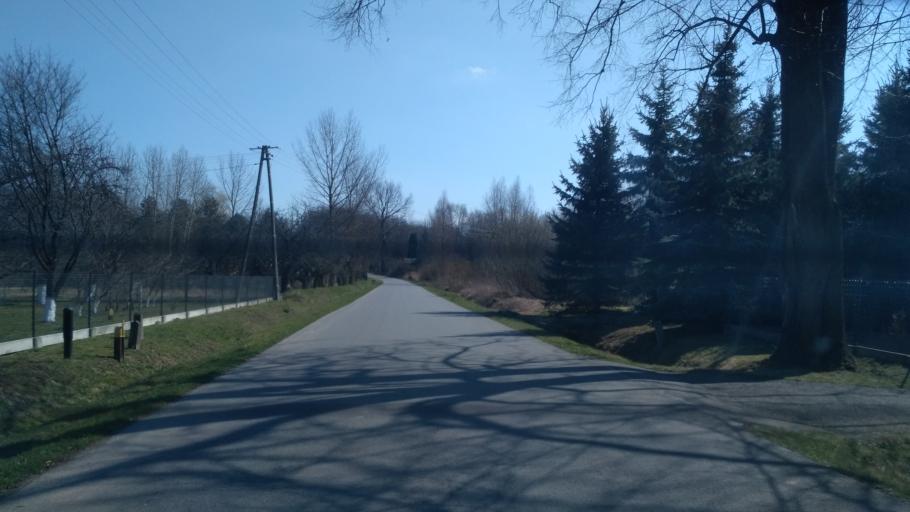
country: PL
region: Subcarpathian Voivodeship
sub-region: Powiat przeworski
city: Pantalowice
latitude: 49.9279
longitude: 22.4447
